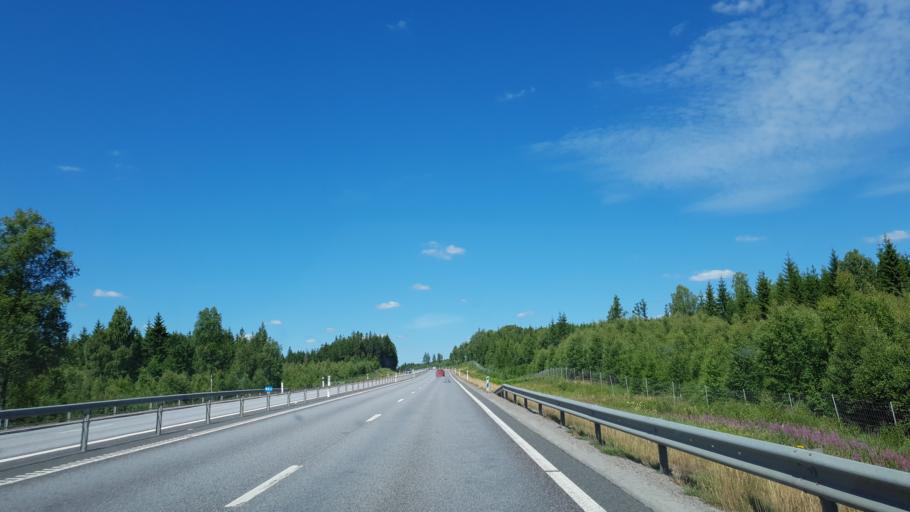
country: SE
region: Kronoberg
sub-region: Vaxjo Kommun
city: Gemla
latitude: 56.9028
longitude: 14.6675
